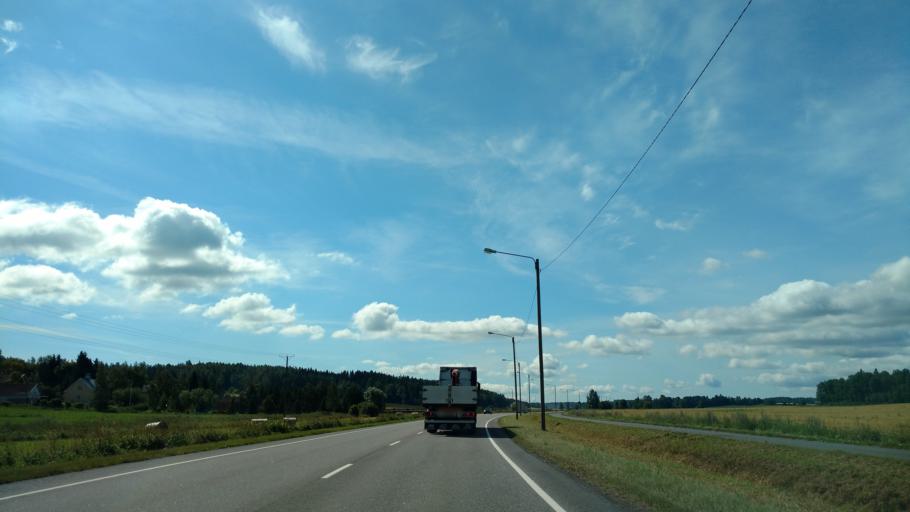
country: FI
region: Varsinais-Suomi
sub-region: Salo
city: Pernioe
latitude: 60.2533
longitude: 23.1351
